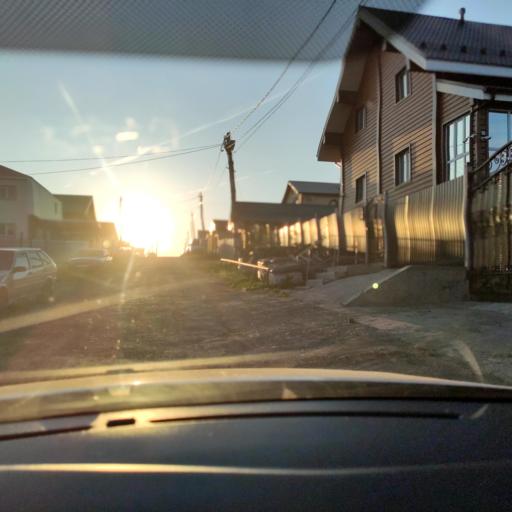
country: RU
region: Tatarstan
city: Stolbishchi
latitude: 55.7516
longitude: 49.3038
